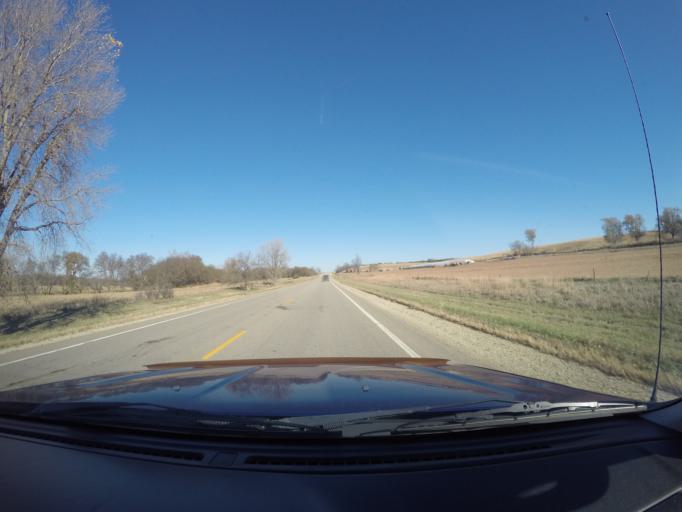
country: US
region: Kansas
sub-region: Riley County
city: Ogden
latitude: 39.3258
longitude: -96.7560
